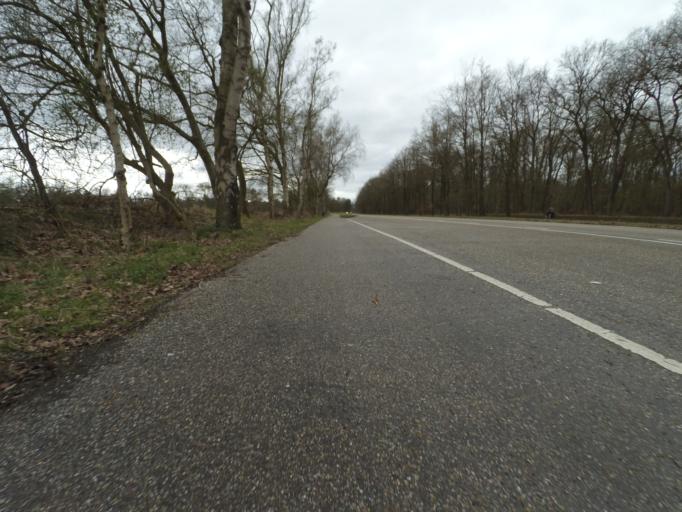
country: NL
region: Gelderland
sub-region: Gemeente Apeldoorn
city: Beekbergen
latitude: 52.1034
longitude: 5.9520
